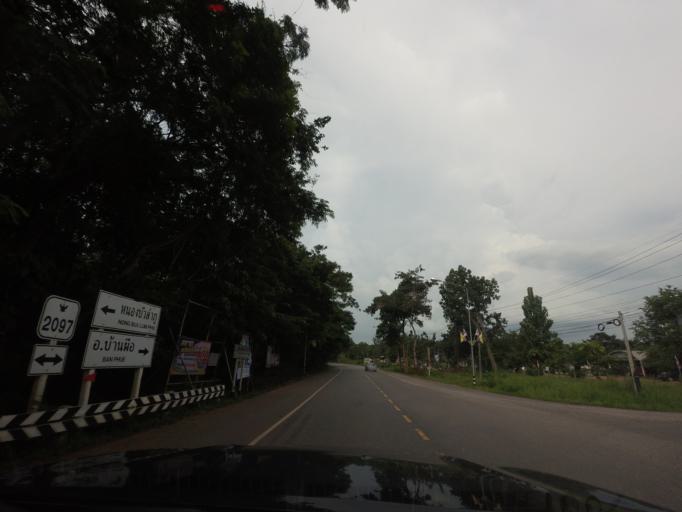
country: TH
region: Changwat Nong Bua Lamphu
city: Suwannakhuha
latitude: 17.4985
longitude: 102.3720
